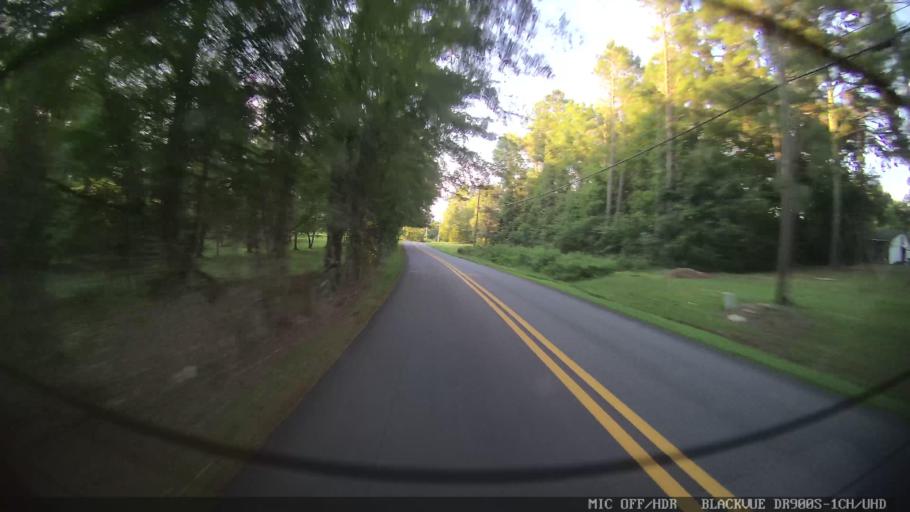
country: US
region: Georgia
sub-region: Bartow County
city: Emerson
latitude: 34.1042
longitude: -84.7145
